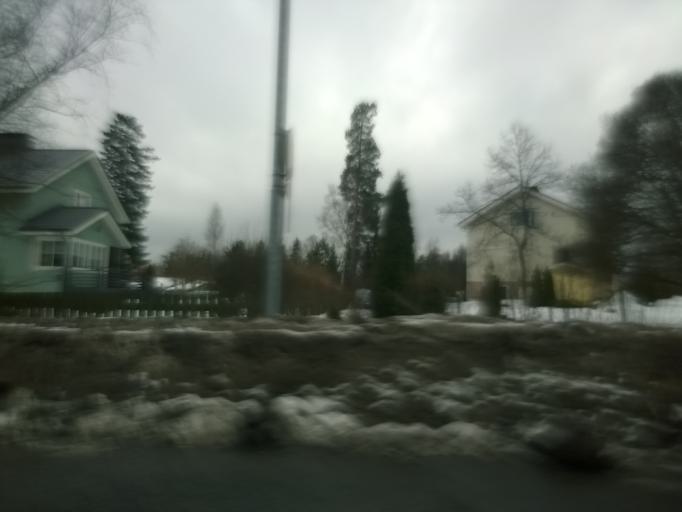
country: FI
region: Pirkanmaa
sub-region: Tampere
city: Tampere
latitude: 61.4139
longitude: 23.7606
